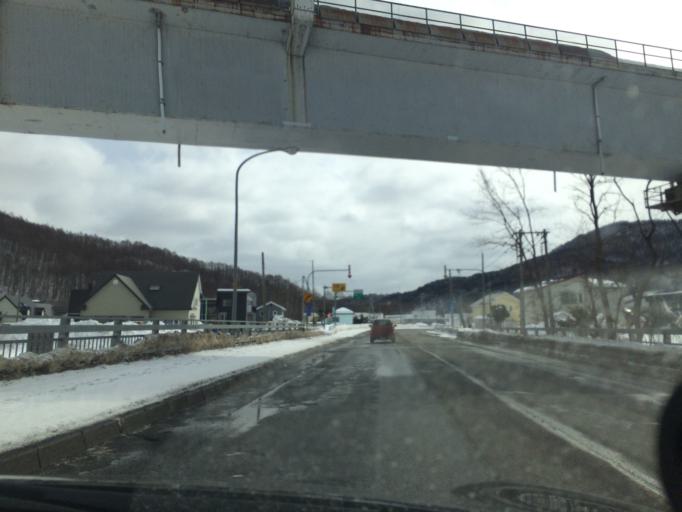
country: JP
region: Hokkaido
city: Iwamizawa
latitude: 42.9430
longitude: 142.0420
